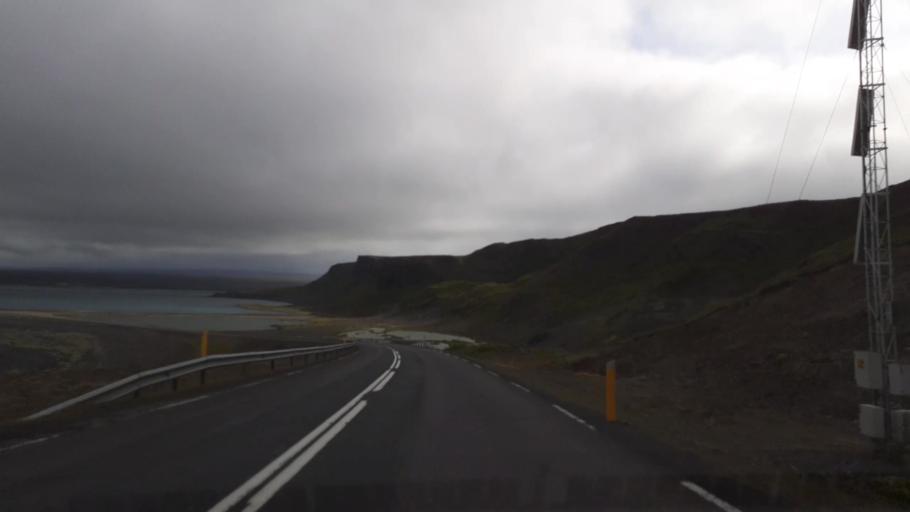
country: IS
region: Northeast
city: Husavik
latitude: 66.1298
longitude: -16.9531
